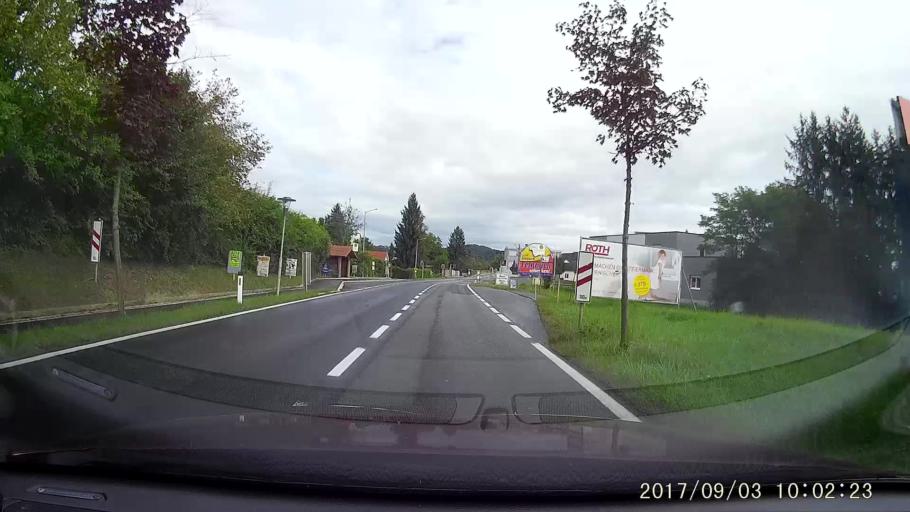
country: AT
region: Styria
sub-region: Politischer Bezirk Suedoststeiermark
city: Muehldorf bei Feldbach
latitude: 46.9437
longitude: 15.9086
